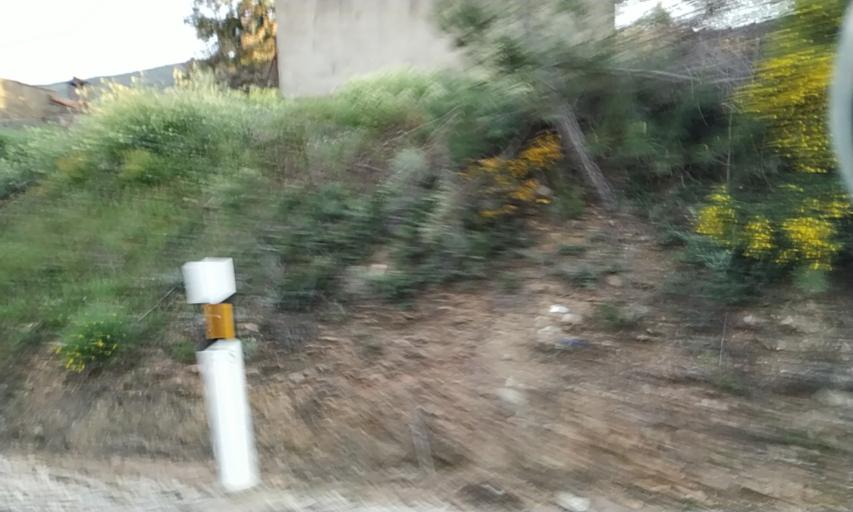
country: PT
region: Portalegre
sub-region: Portalegre
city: Sao Juliao
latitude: 39.3469
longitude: -7.2994
